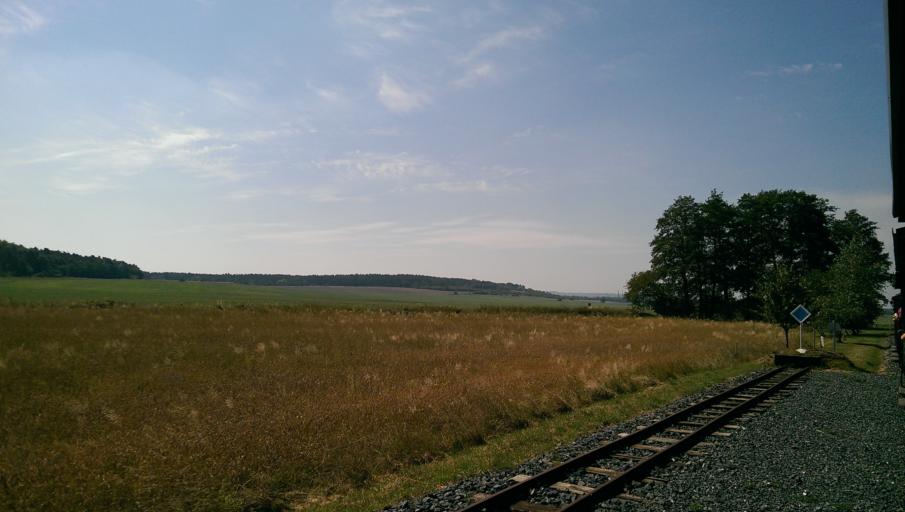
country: CZ
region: Central Bohemia
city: Stary Kolin
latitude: 50.0529
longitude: 15.2545
